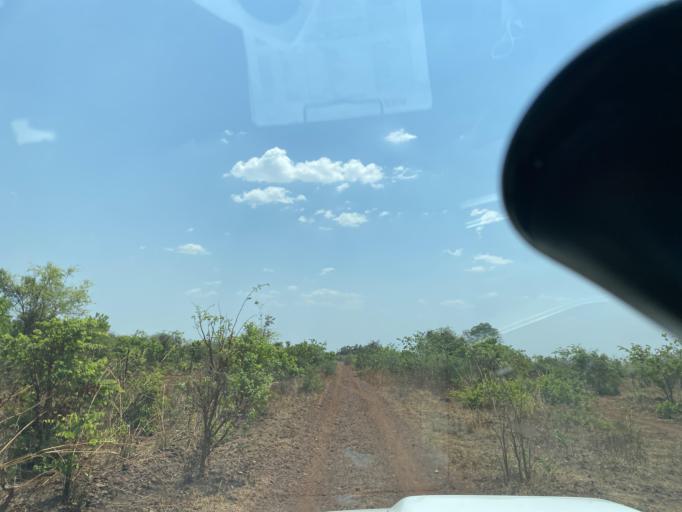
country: ZM
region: Lusaka
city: Lusaka
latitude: -15.4976
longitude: 27.9666
